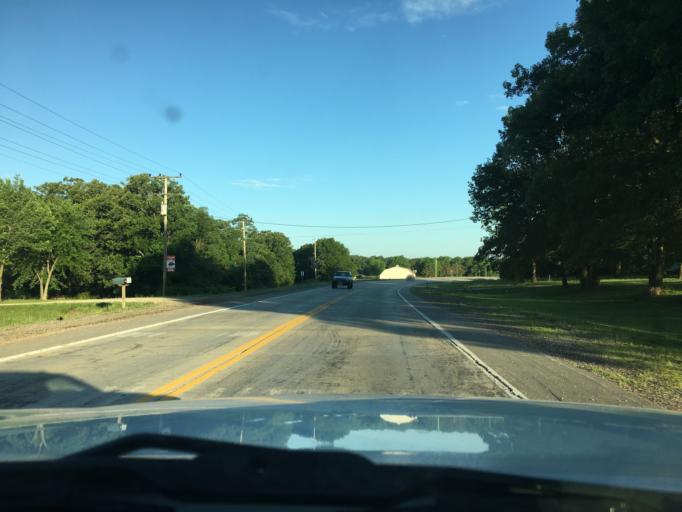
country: US
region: Missouri
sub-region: Franklin County
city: Gerald
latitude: 38.3875
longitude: -91.4128
